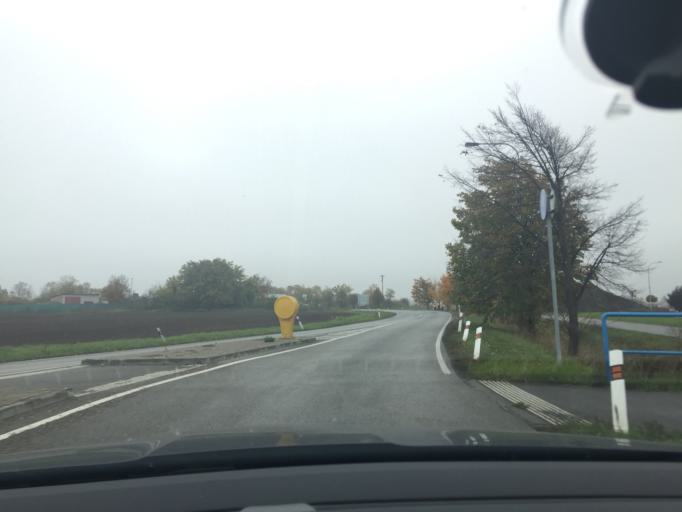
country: CZ
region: South Moravian
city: Rousinov
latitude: 49.1976
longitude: 16.8791
